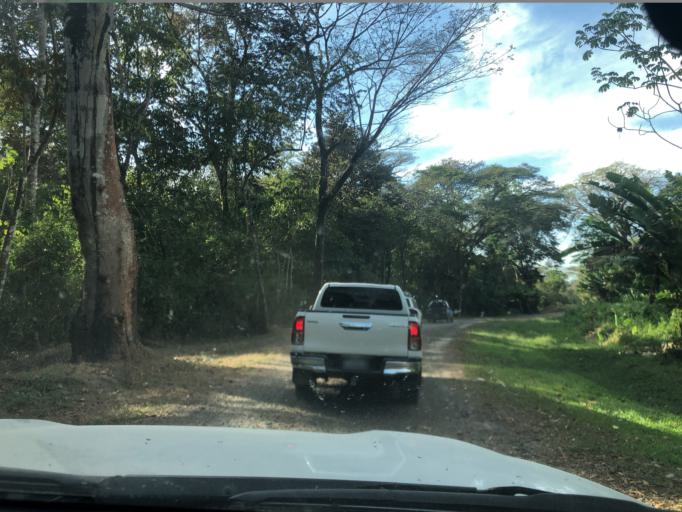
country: CR
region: Alajuela
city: San Jose
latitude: 11.1089
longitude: -85.2801
